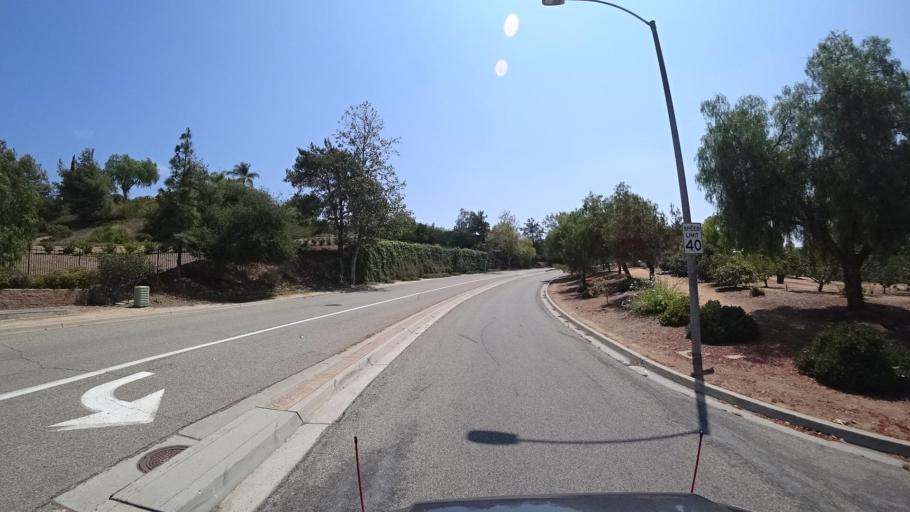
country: US
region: California
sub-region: San Diego County
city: Bonsall
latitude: 33.3173
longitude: -117.2175
